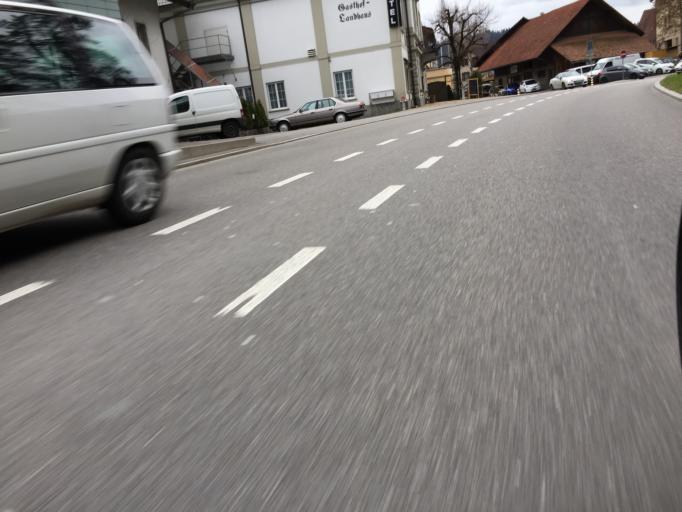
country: CH
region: Bern
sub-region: Emmental District
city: Burgdorf
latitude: 47.0544
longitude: 7.6298
